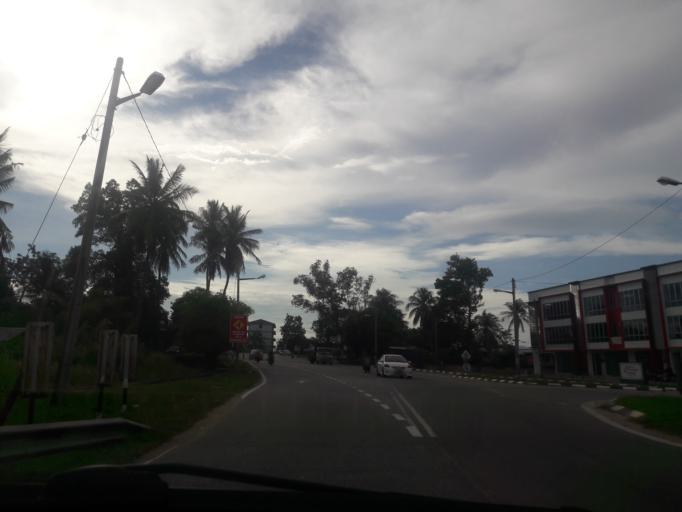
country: MY
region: Kedah
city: Sungai Petani
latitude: 5.6277
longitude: 100.5268
